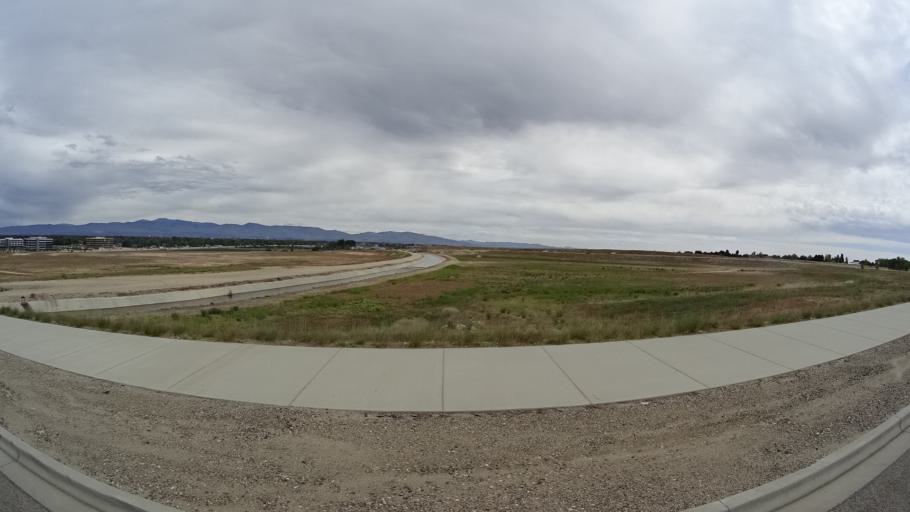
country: US
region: Idaho
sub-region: Ada County
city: Meridian
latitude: 43.5877
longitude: -116.4337
